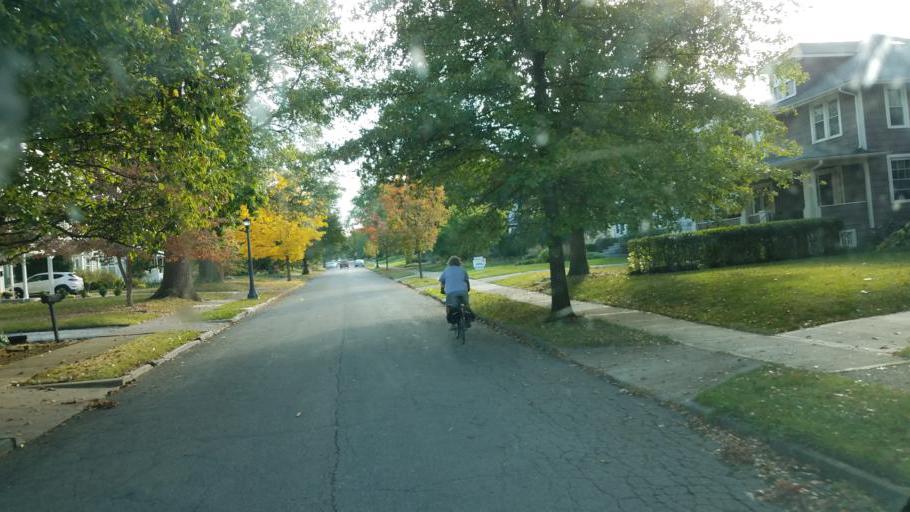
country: US
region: Ohio
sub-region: Franklin County
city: Worthington
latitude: 40.0351
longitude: -83.0112
